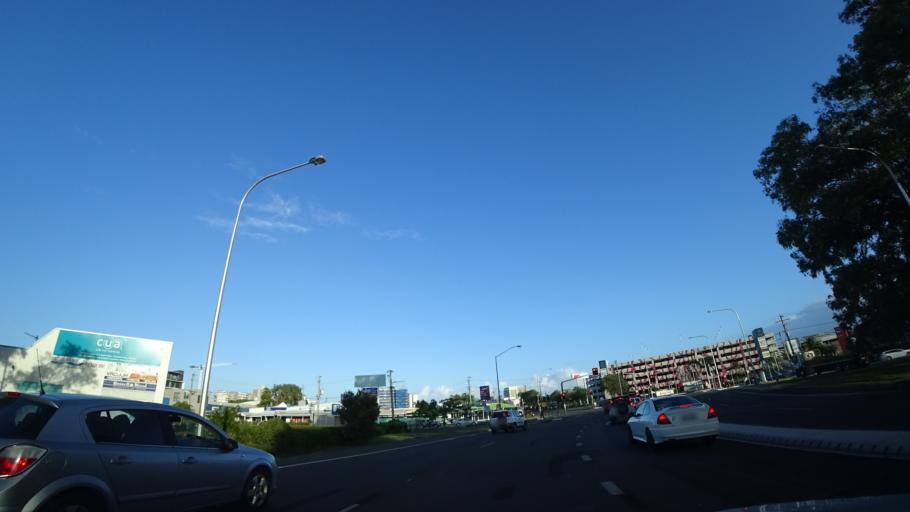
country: AU
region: Queensland
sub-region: Sunshine Coast
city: Buderim
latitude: -26.6521
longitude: 153.0865
